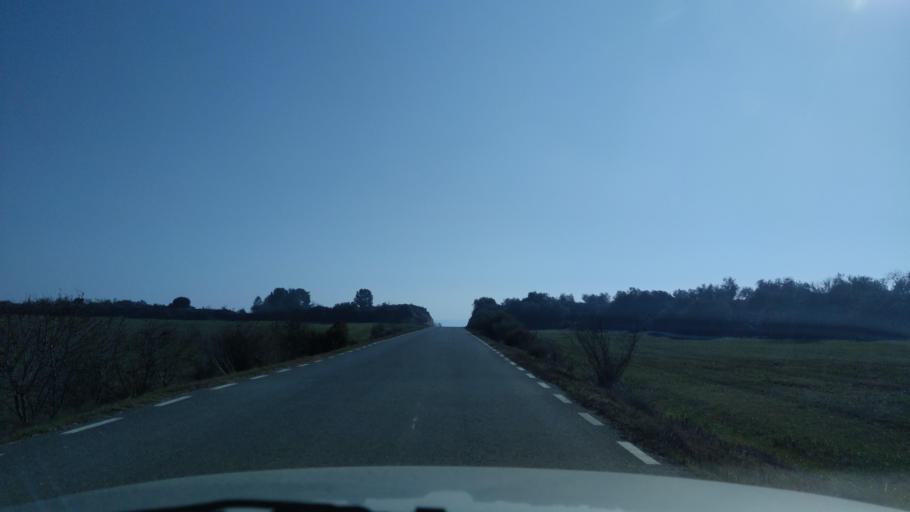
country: ES
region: Catalonia
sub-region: Provincia de Lleida
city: Torrebesses
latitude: 41.4686
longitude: 0.5626
